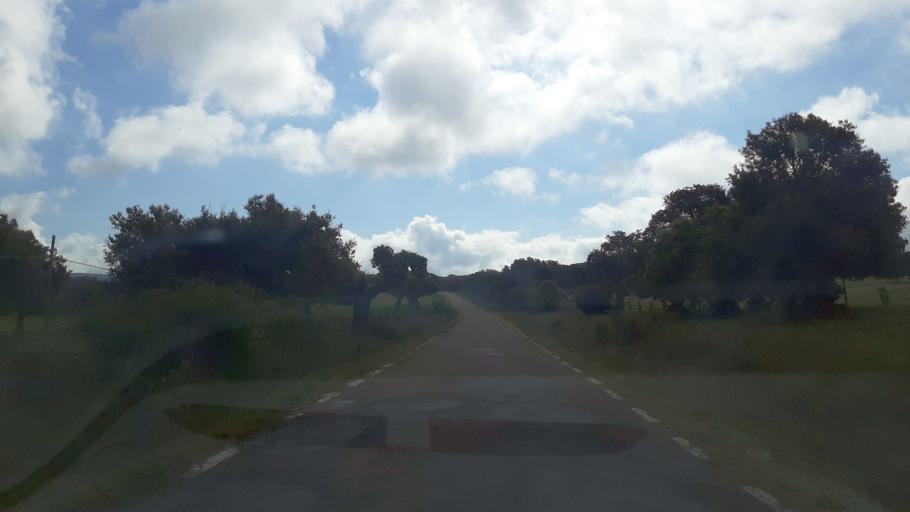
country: ES
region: Castille and Leon
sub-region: Provincia de Salamanca
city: Narros de Matalayegua
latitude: 40.7034
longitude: -5.9137
